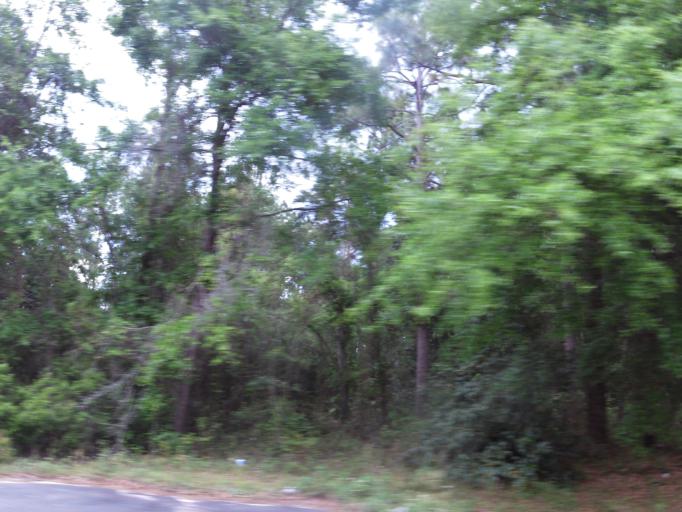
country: US
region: Georgia
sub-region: Charlton County
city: Folkston
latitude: 30.8435
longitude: -82.0000
